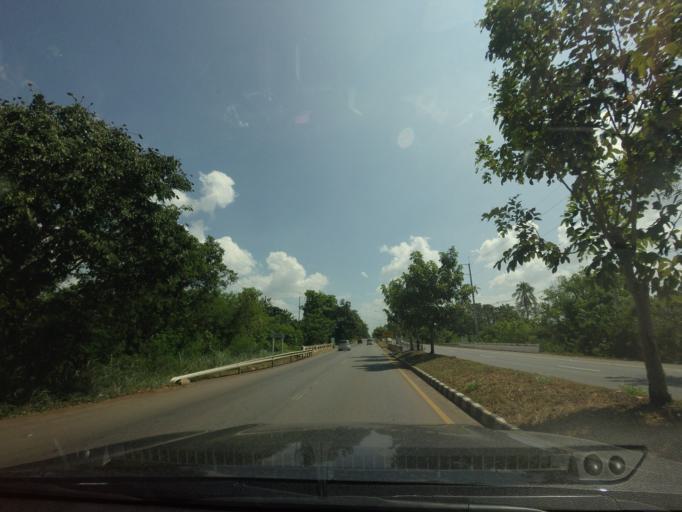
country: TH
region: Phetchabun
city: Nong Phai
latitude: 16.0625
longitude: 101.0726
